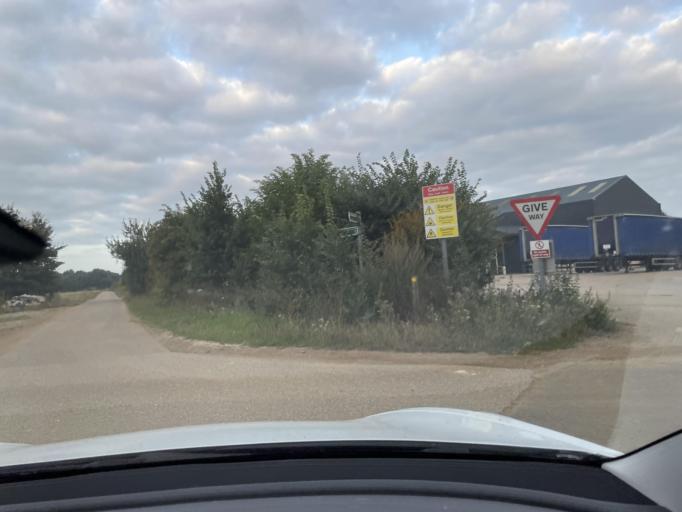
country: GB
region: England
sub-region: Cambridgeshire
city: Duxford
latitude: 52.0944
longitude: 0.1108
